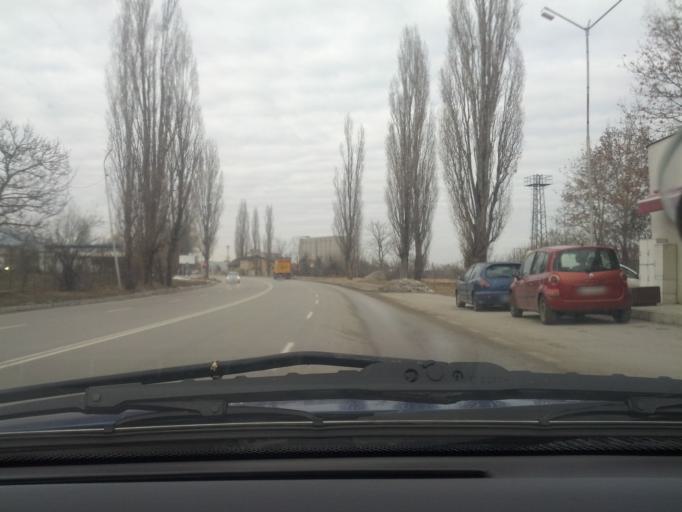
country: BG
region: Vratsa
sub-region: Obshtina Vratsa
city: Vratsa
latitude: 43.2041
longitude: 23.5704
